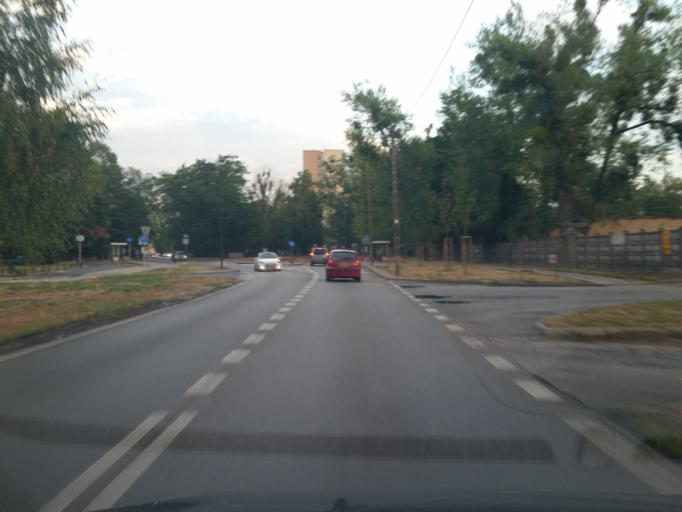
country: PL
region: Masovian Voivodeship
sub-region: Warszawa
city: Bemowo
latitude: 52.2557
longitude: 20.9045
